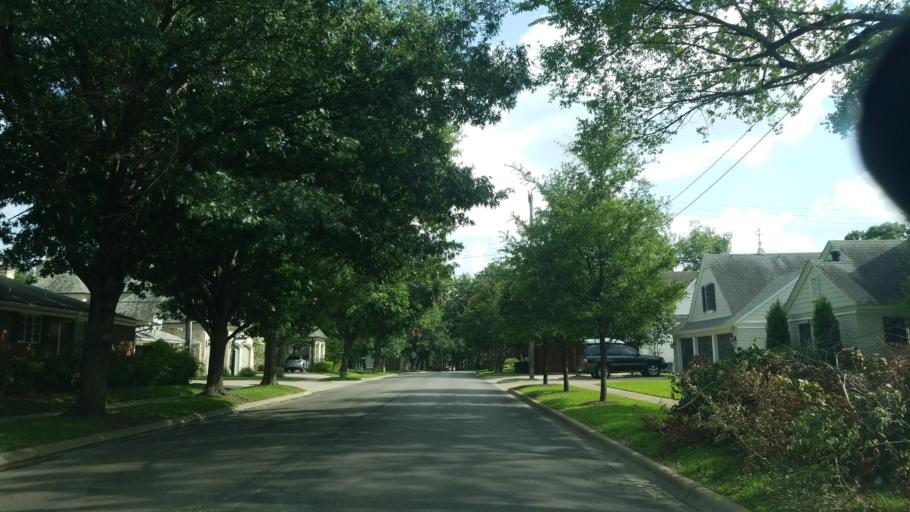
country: US
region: Texas
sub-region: Dallas County
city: University Park
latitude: 32.8643
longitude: -96.7921
